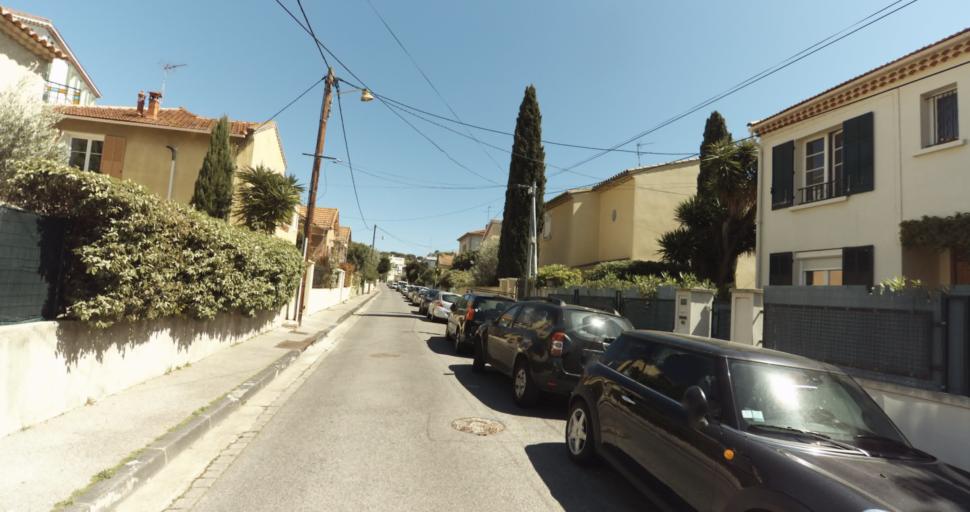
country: FR
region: Provence-Alpes-Cote d'Azur
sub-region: Departement du Var
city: Toulon
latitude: 43.1144
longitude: 5.9479
